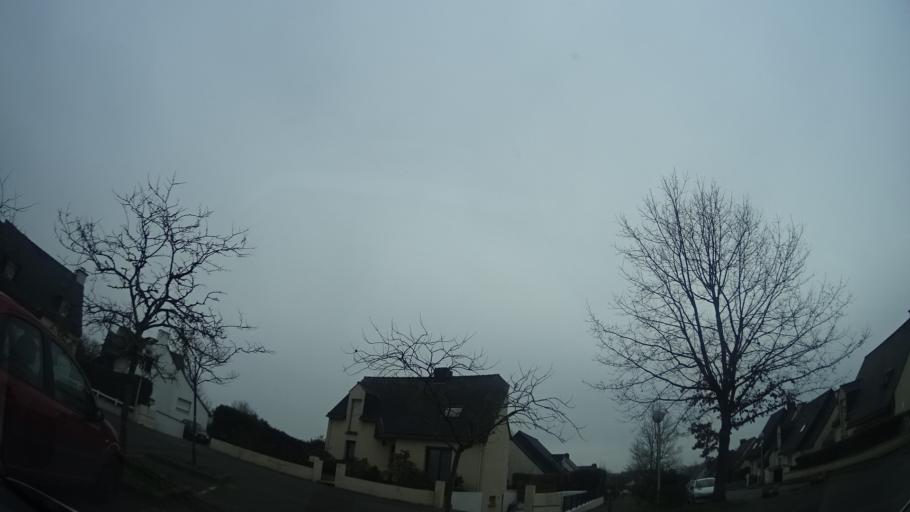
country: FR
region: Brittany
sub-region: Departement d'Ille-et-Vilaine
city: Brece
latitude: 48.1084
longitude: -1.4776
